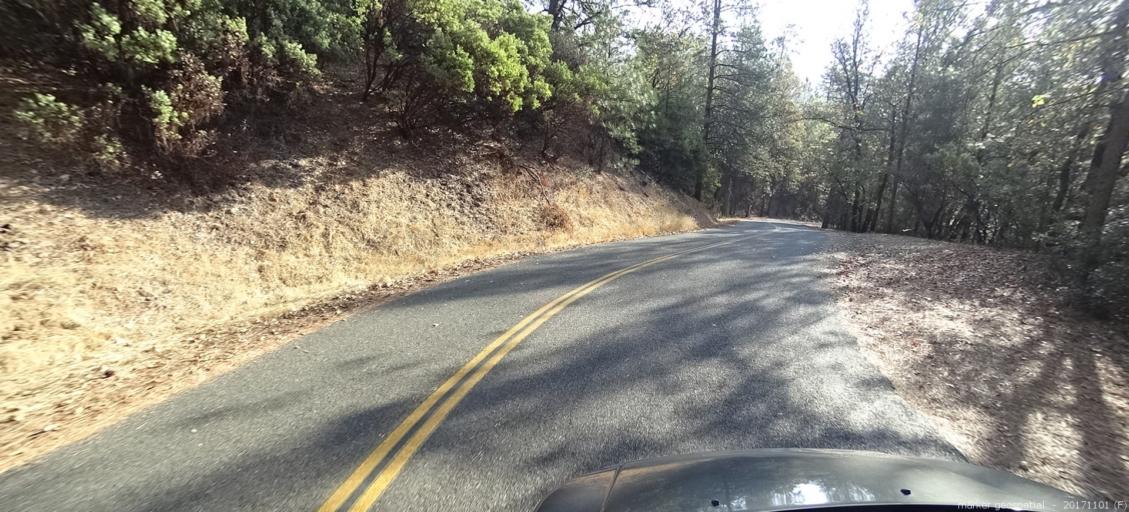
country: US
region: California
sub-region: Shasta County
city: Shasta Lake
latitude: 40.8053
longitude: -122.3059
